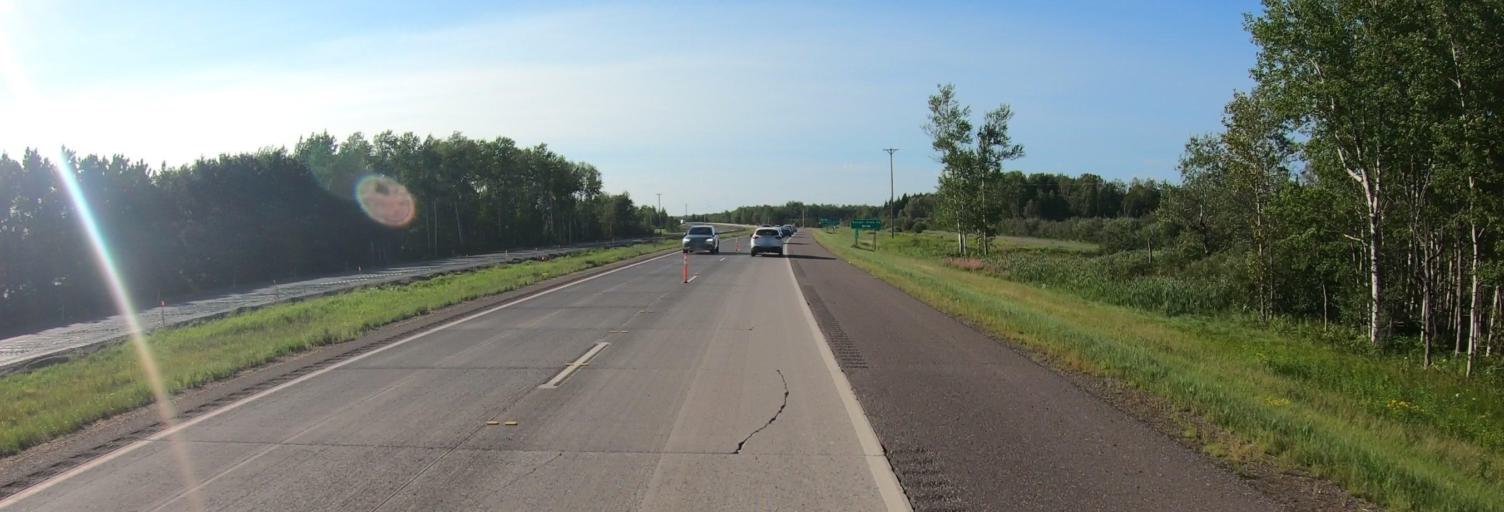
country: US
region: Minnesota
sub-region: Saint Louis County
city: Hermantown
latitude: 46.8760
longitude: -92.3436
